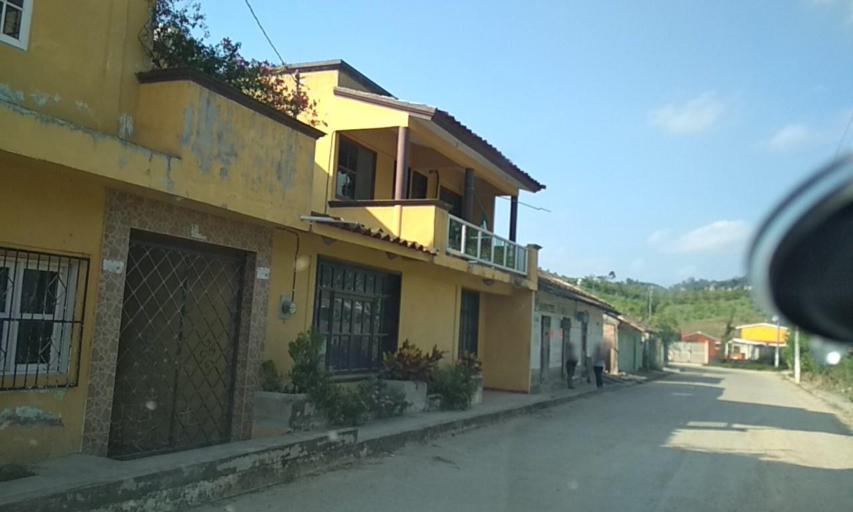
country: MX
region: Veracruz
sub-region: Papantla
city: Polutla
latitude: 20.5980
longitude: -97.2567
